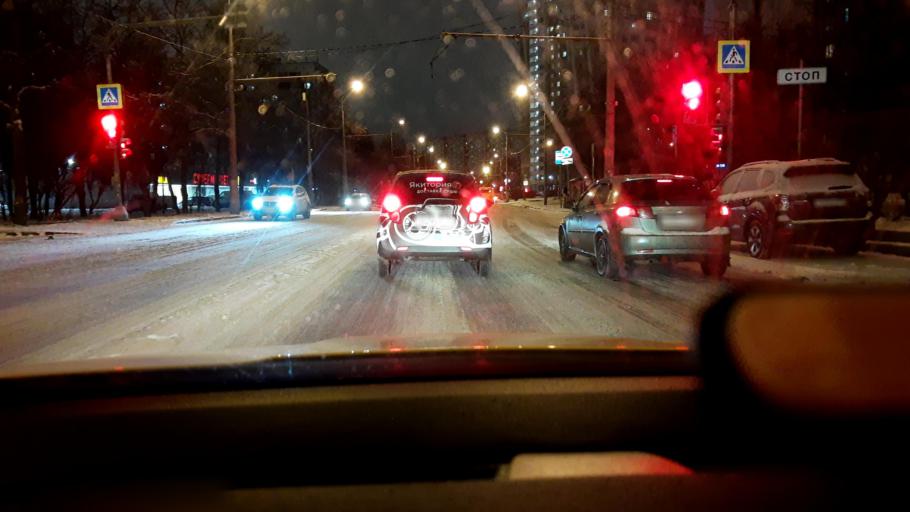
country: RU
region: Moscow
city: Strogino
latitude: 55.8501
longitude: 37.4155
